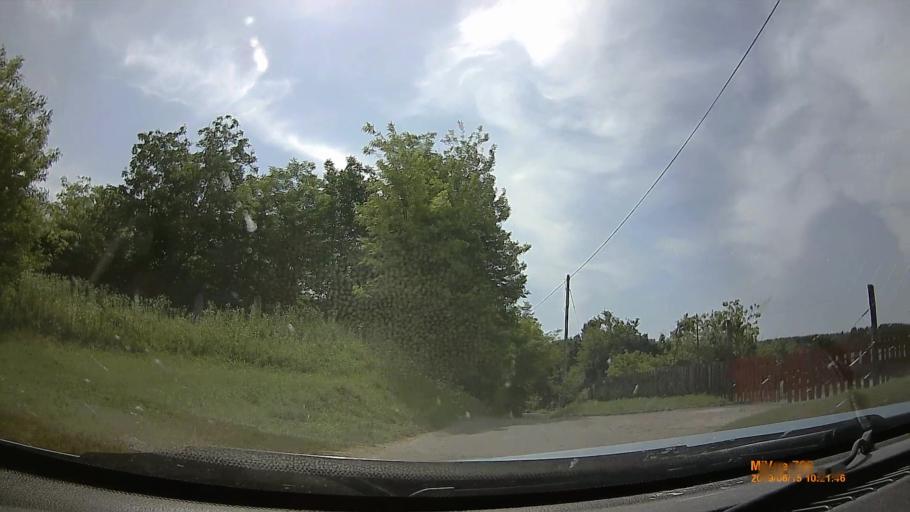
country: HU
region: Baranya
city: Buekkoesd
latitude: 46.1093
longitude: 18.0070
